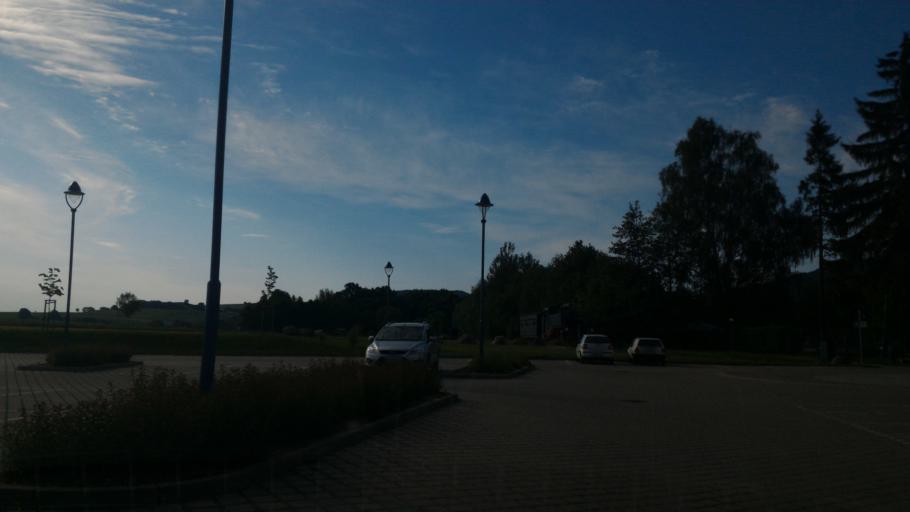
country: DE
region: Saxony
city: Grossschonau
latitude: 50.8812
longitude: 14.6705
